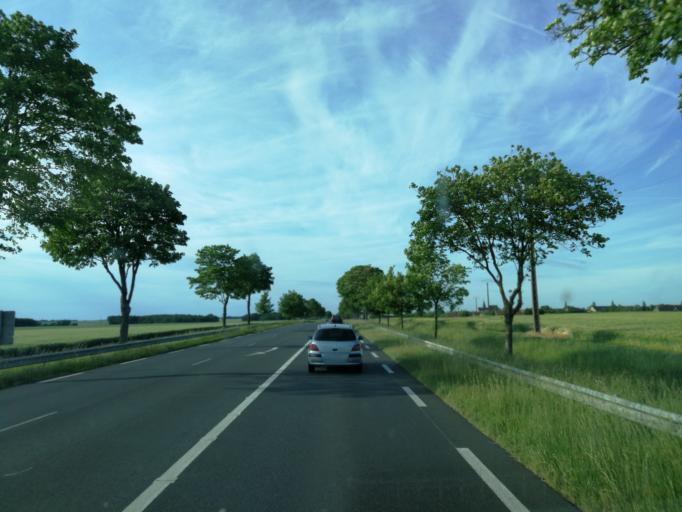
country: FR
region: Centre
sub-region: Departement d'Eure-et-Loir
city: Bonneval
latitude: 48.2691
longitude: 1.4156
